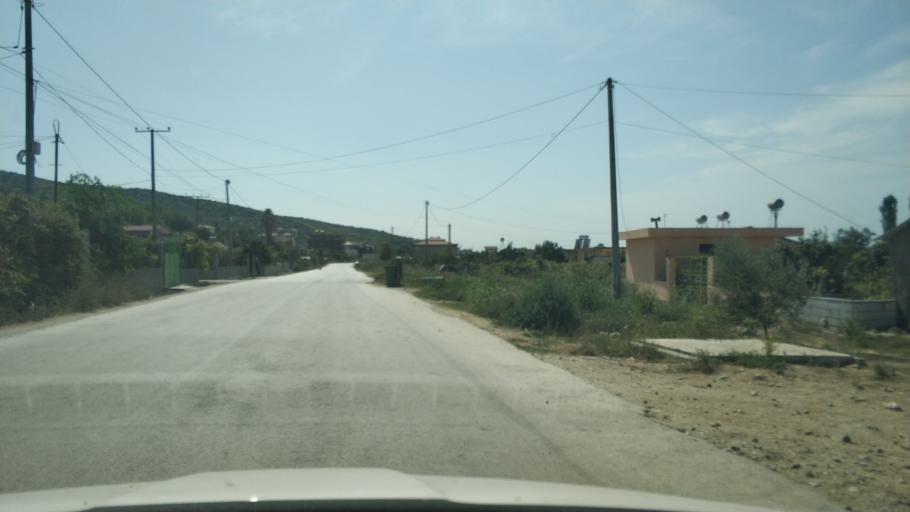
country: AL
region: Fier
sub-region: Rrethi i Lushnjes
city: Grabjan
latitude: 40.9433
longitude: 19.5374
